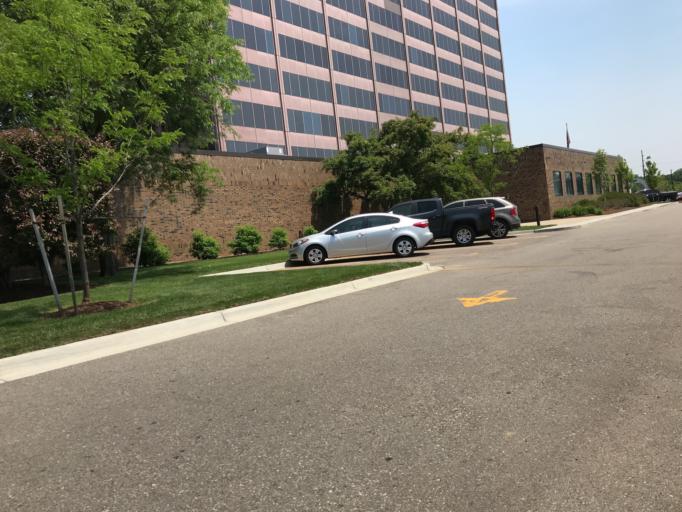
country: US
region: Michigan
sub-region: Oakland County
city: Southfield
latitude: 42.4834
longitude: -83.2439
